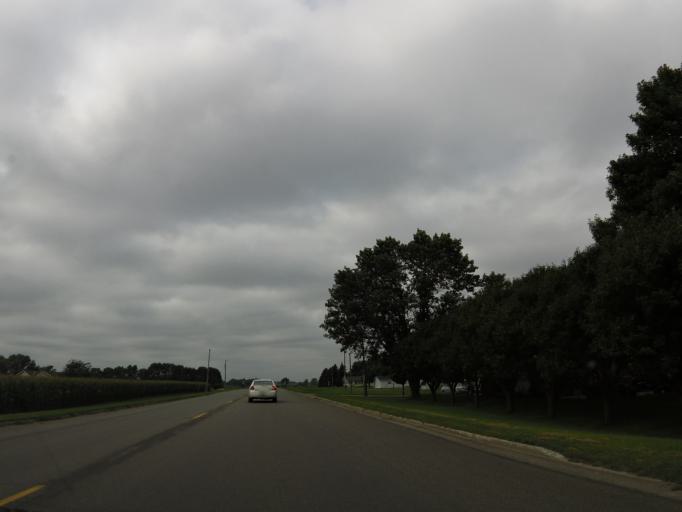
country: US
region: Minnesota
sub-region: Renville County
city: Renville
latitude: 44.7889
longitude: -95.1040
